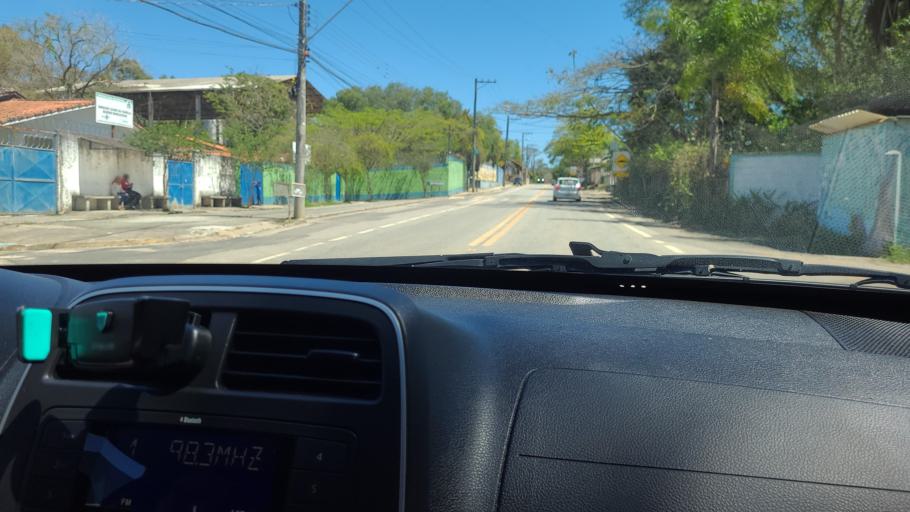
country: BR
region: Sao Paulo
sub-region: Tremembe
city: Tremembe
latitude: -22.8870
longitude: -45.5453
